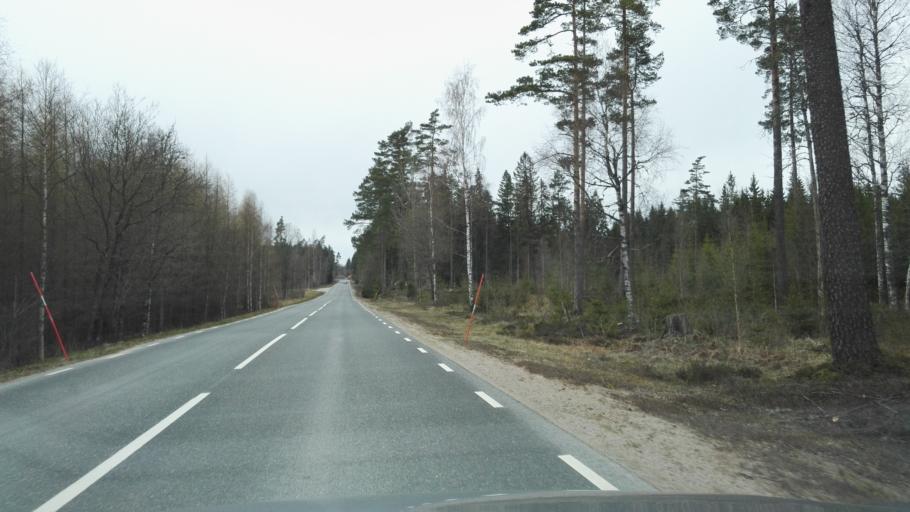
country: SE
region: Joenkoeping
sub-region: Vetlanda Kommun
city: Landsbro
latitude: 57.2517
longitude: 14.9444
